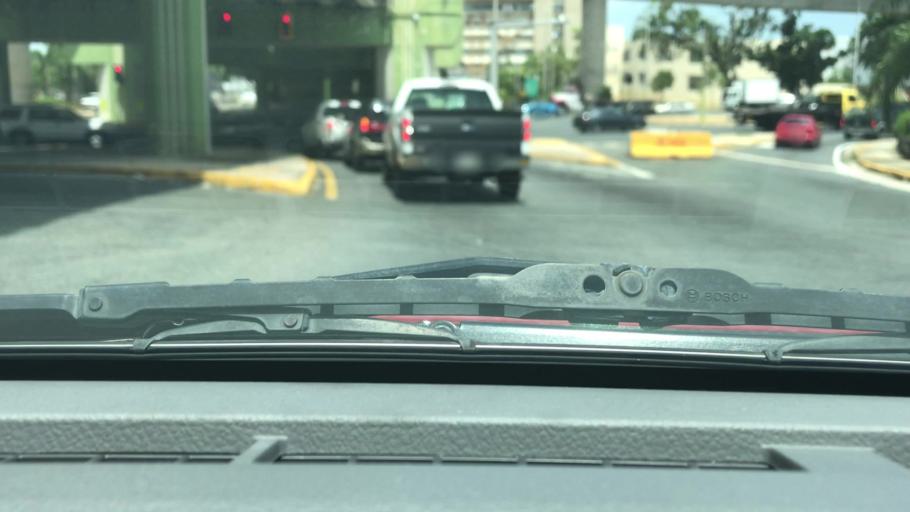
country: PR
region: Bayamon
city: Bayamon
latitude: 18.3960
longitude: -66.1531
